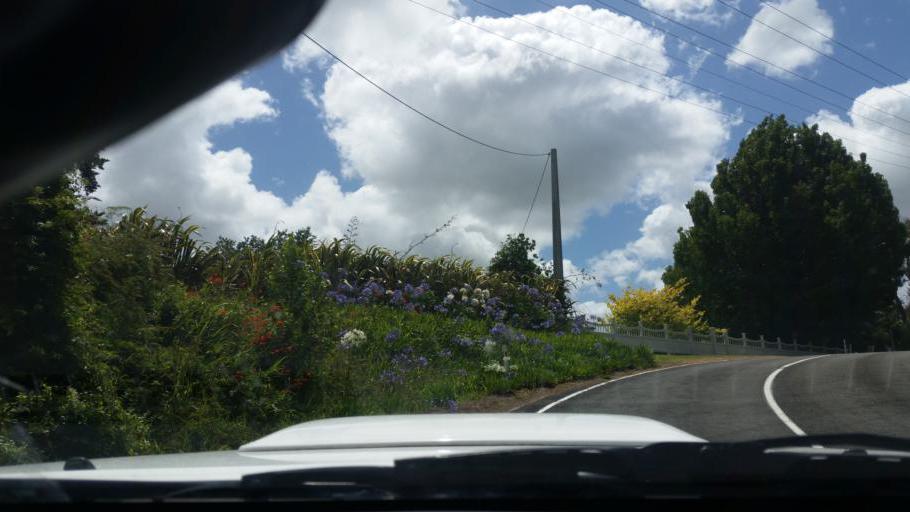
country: NZ
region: Northland
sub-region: Whangarei
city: Ruakaka
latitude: -36.0990
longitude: 174.2322
